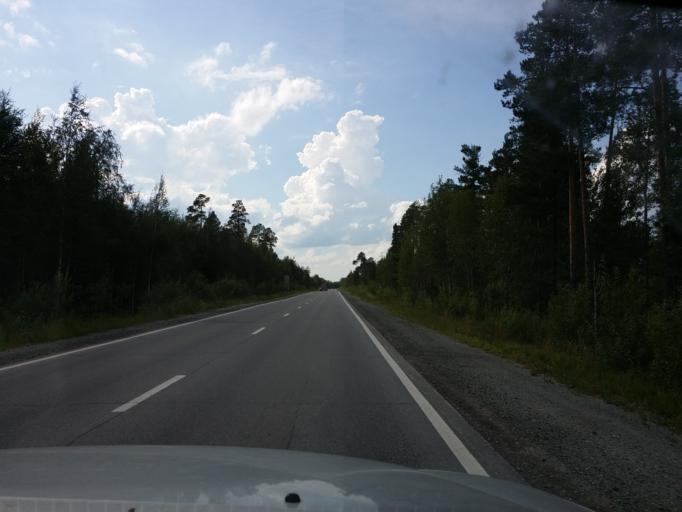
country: RU
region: Khanty-Mansiyskiy Avtonomnyy Okrug
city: Megion
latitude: 61.1266
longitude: 75.8113
